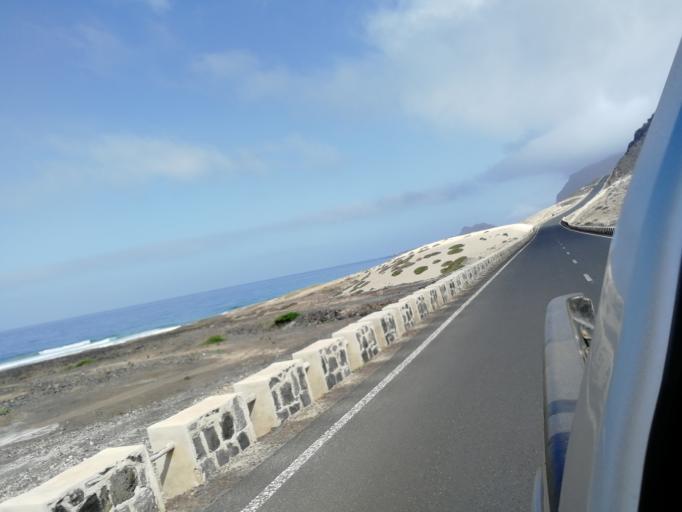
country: CV
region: Sao Vicente
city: Mindelo
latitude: 16.8729
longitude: -24.9075
